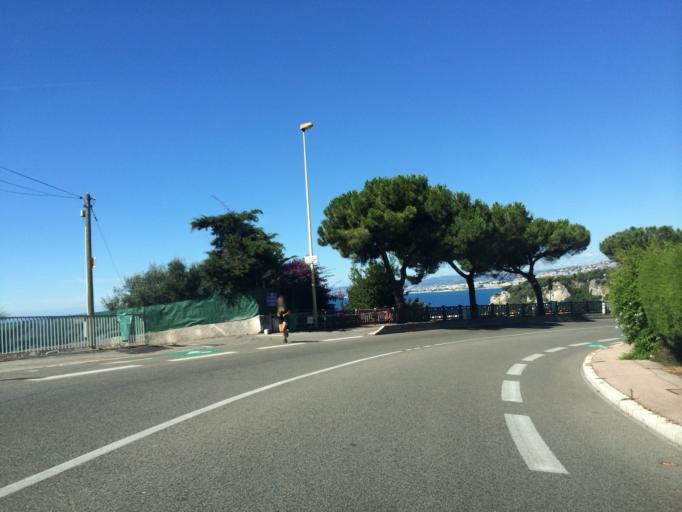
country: FR
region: Provence-Alpes-Cote d'Azur
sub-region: Departement des Alpes-Maritimes
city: Villefranche-sur-Mer
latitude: 43.6974
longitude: 7.2949
